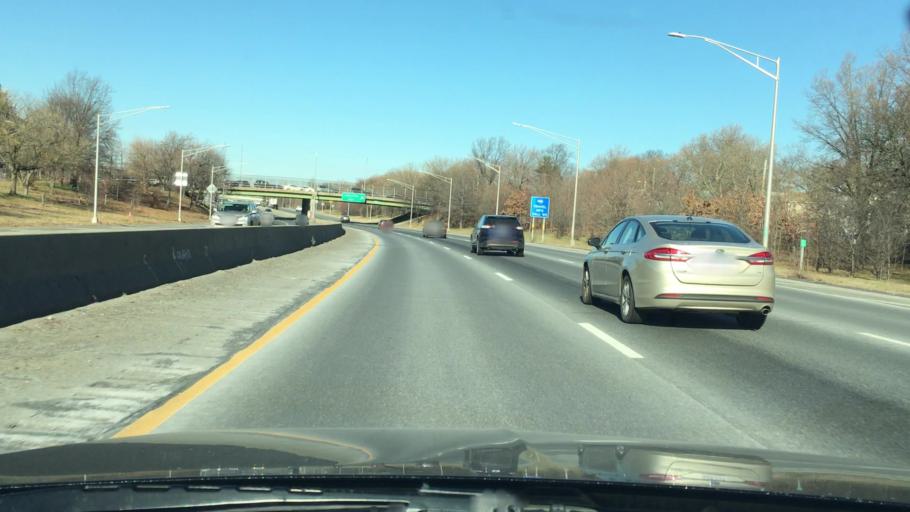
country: US
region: New York
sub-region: Bronx
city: The Bronx
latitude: 40.8266
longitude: -73.8169
